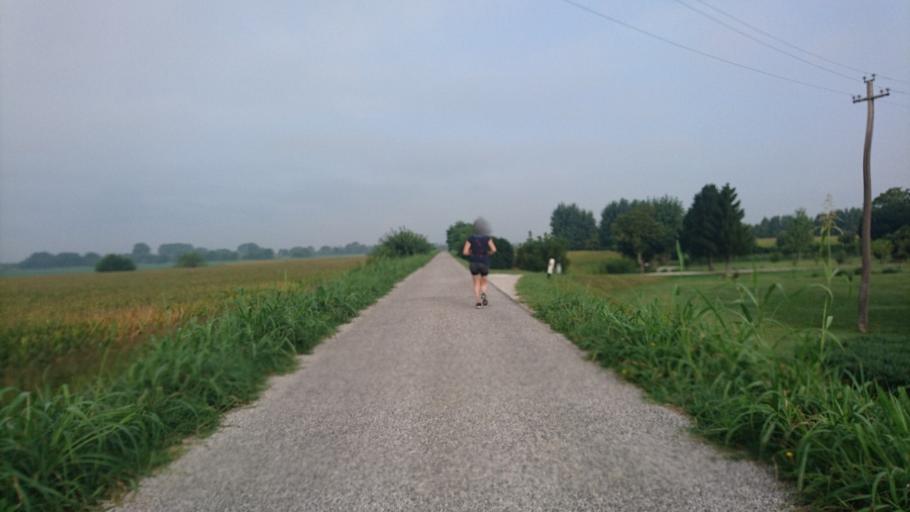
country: IT
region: Veneto
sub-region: Provincia di Padova
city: Selvazzano Dentro
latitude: 45.3989
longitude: 11.7755
